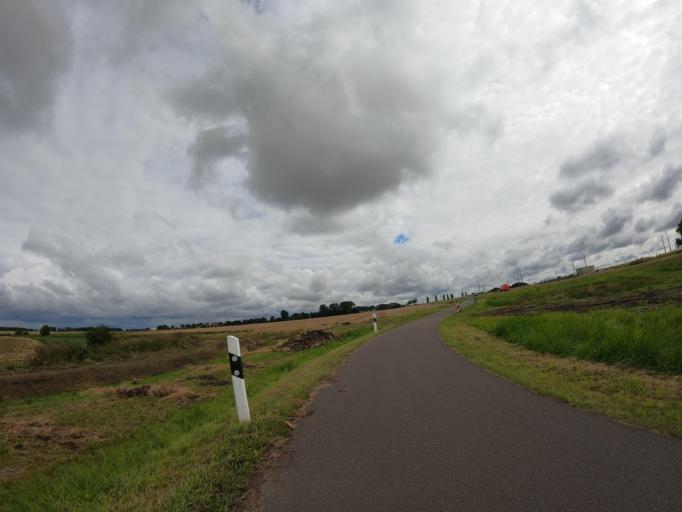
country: DE
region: Mecklenburg-Vorpommern
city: Rambin
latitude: 54.3471
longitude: 13.1720
